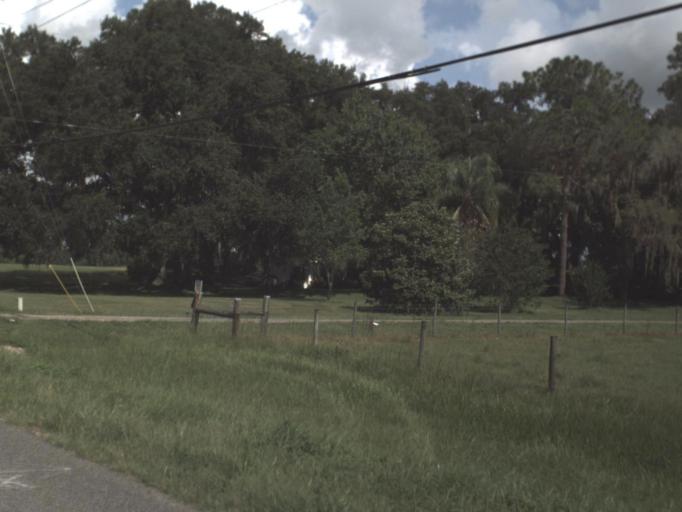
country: US
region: Florida
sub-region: Pasco County
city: San Antonio
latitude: 28.3320
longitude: -82.2937
